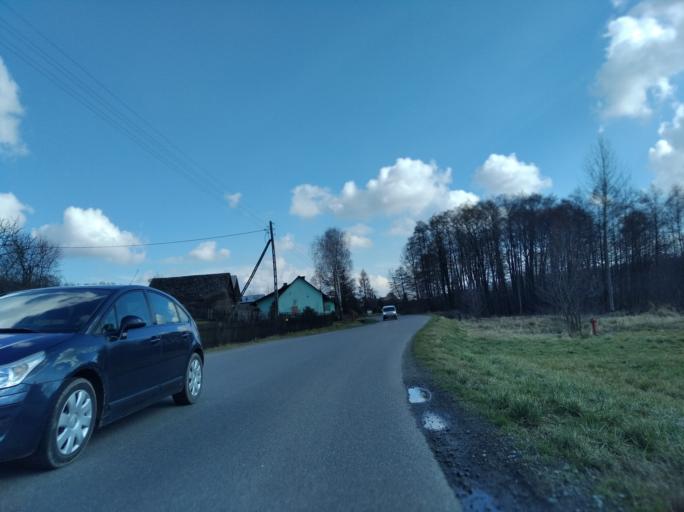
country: PL
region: Subcarpathian Voivodeship
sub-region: Powiat debicki
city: Brzostek
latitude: 49.8621
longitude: 21.4657
